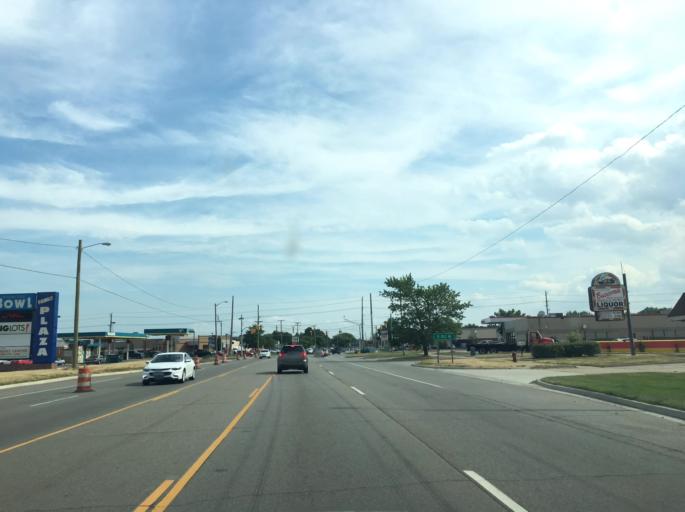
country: US
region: Michigan
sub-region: Macomb County
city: Fraser
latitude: 42.5393
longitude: -82.9892
